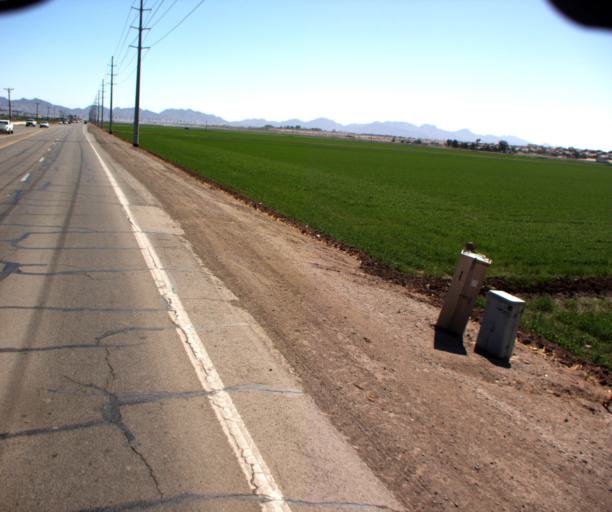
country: US
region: Arizona
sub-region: Yuma County
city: Yuma
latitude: 32.6991
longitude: -114.5280
